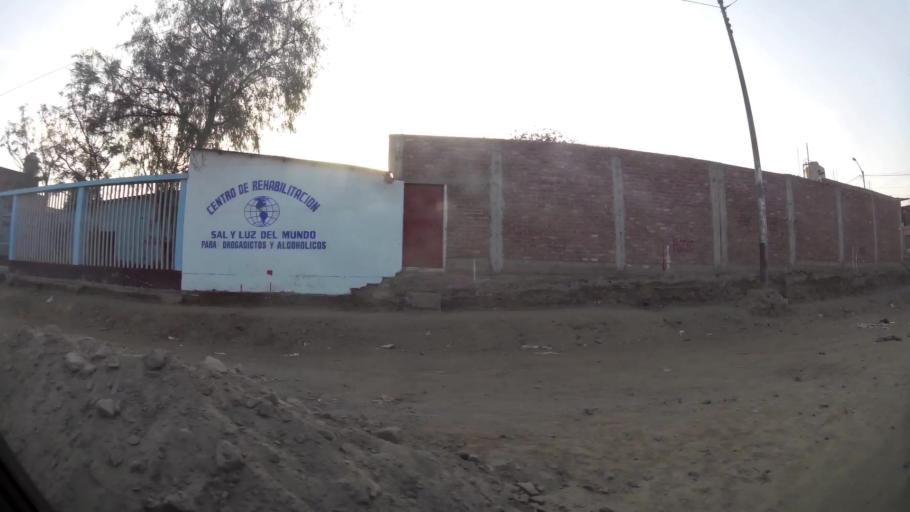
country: PE
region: La Libertad
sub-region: Provincia de Trujillo
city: El Porvenir
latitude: -8.0675
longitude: -78.9961
